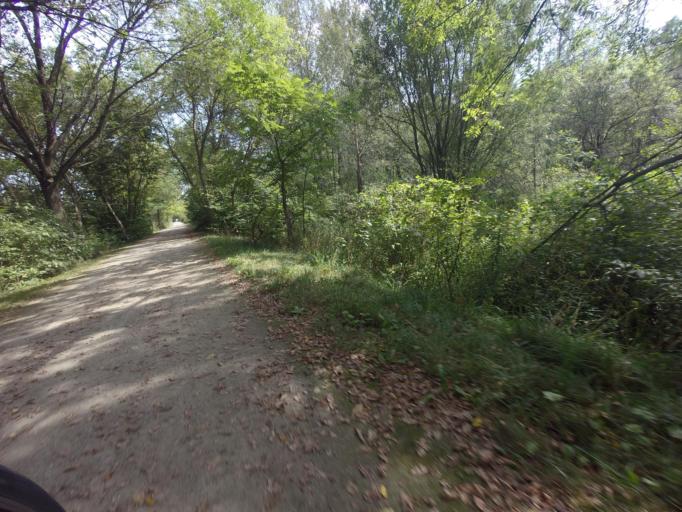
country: CA
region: Ontario
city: Waterloo
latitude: 43.6060
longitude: -80.5601
